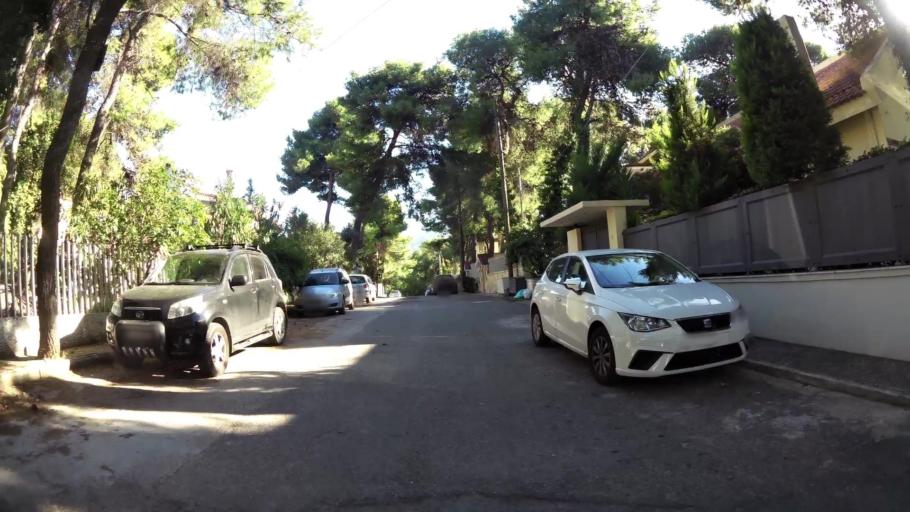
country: GR
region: Attica
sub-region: Nomarchia Athinas
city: Ekali
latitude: 38.1223
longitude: 23.8449
